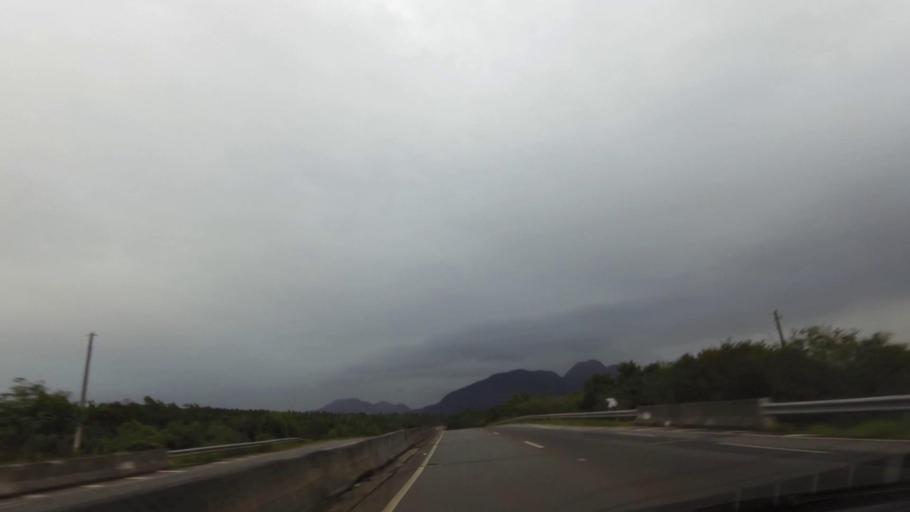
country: BR
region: Espirito Santo
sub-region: Guarapari
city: Guarapari
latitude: -20.6112
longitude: -40.4609
